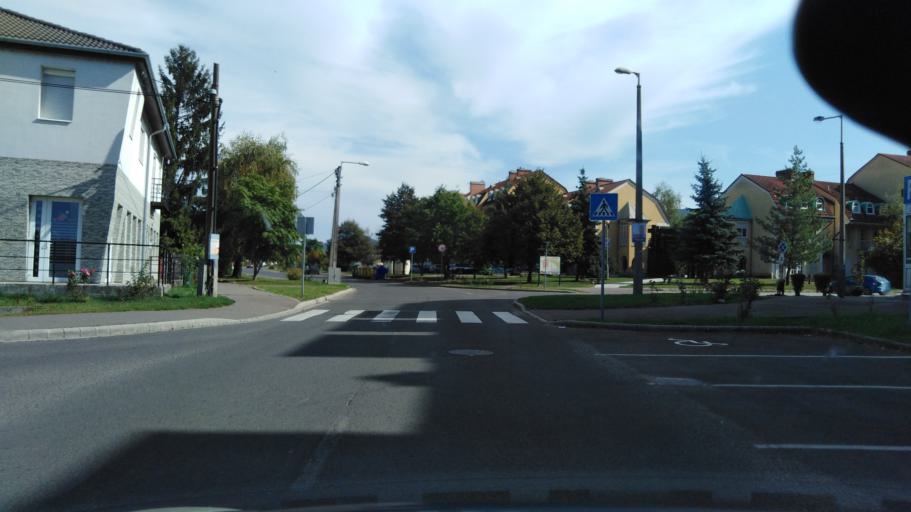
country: HU
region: Nograd
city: Paszto
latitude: 47.9212
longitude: 19.6949
